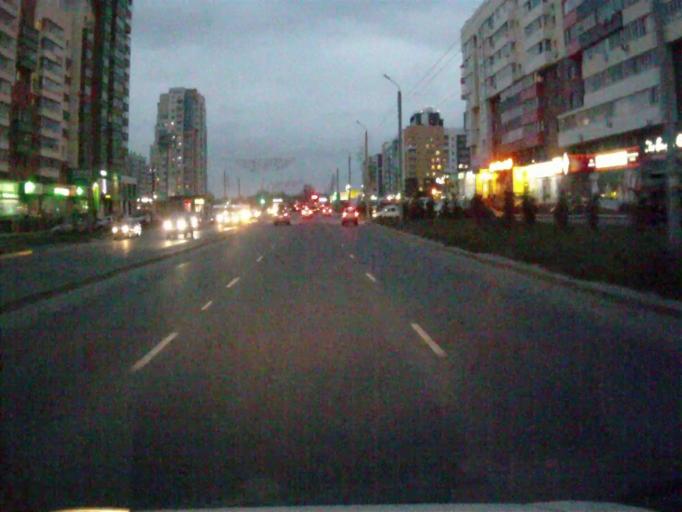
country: RU
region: Chelyabinsk
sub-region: Gorod Chelyabinsk
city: Chelyabinsk
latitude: 55.1651
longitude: 61.2949
